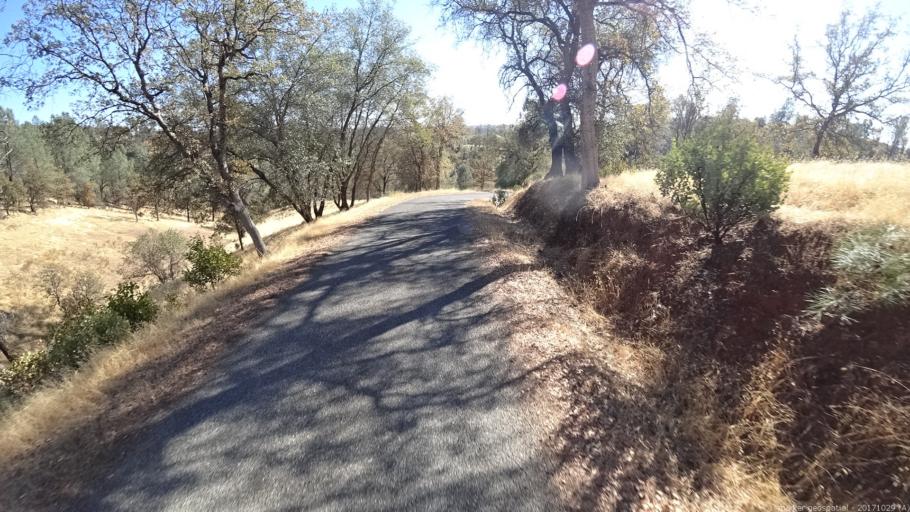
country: US
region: California
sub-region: Shasta County
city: Shasta
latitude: 40.4782
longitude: -122.6224
